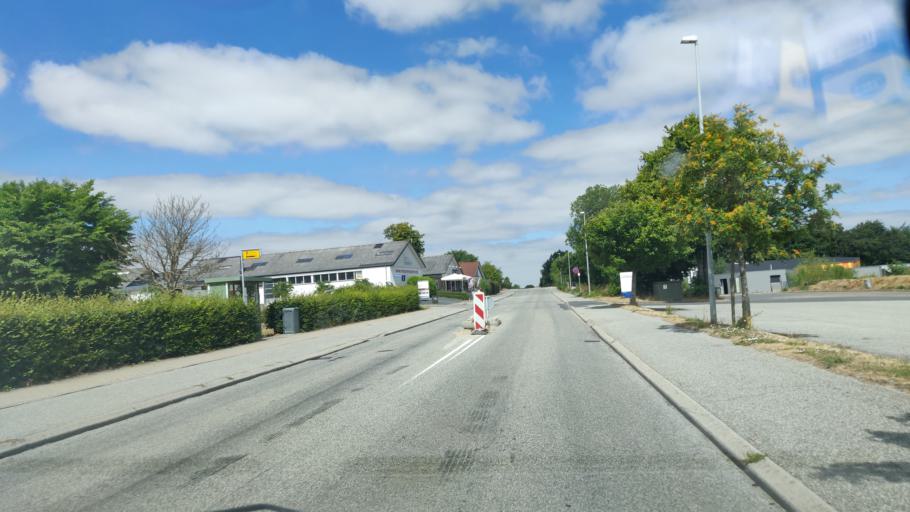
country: DK
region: South Denmark
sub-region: Fredericia Kommune
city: Taulov
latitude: 55.5335
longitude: 9.6209
